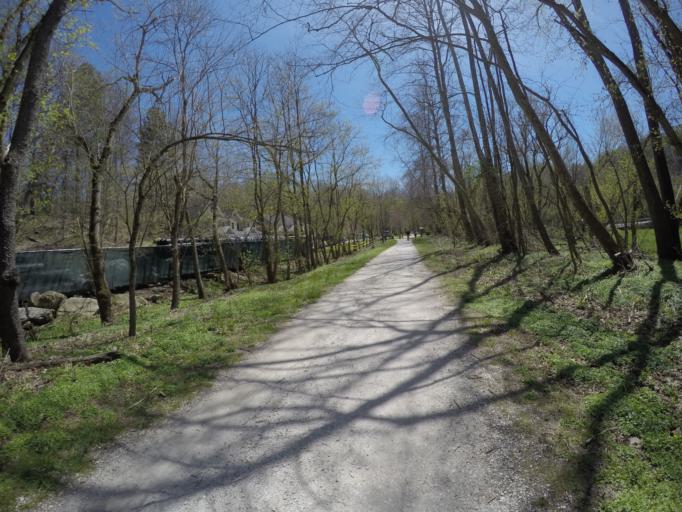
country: US
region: Maryland
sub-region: Baltimore County
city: Hunt Valley
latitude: 39.5407
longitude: -76.6386
